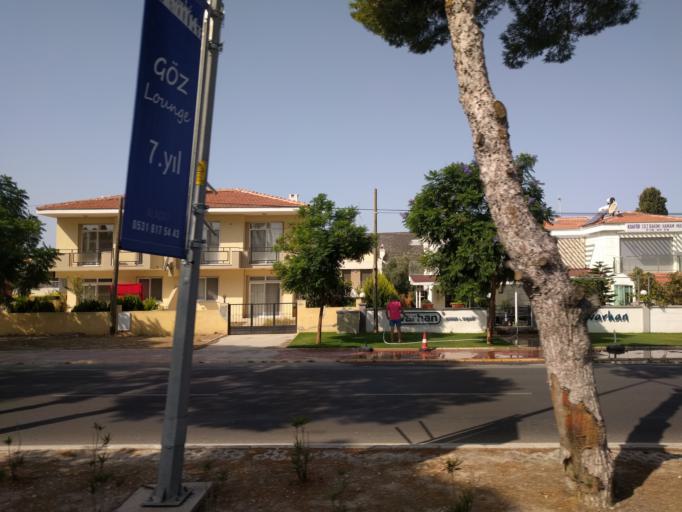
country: TR
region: Izmir
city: Alacati
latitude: 38.2910
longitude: 26.3683
